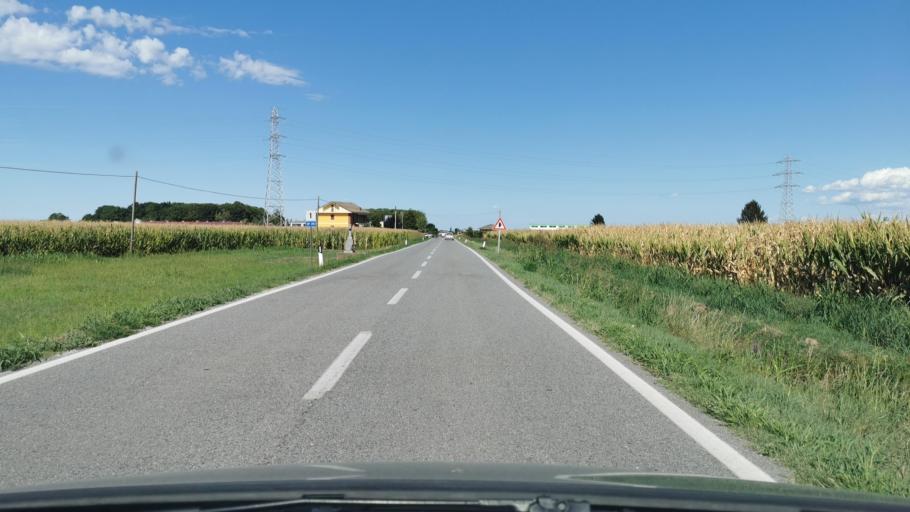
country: IT
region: Piedmont
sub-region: Provincia di Cuneo
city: Tarantasca
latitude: 44.4973
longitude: 7.5648
